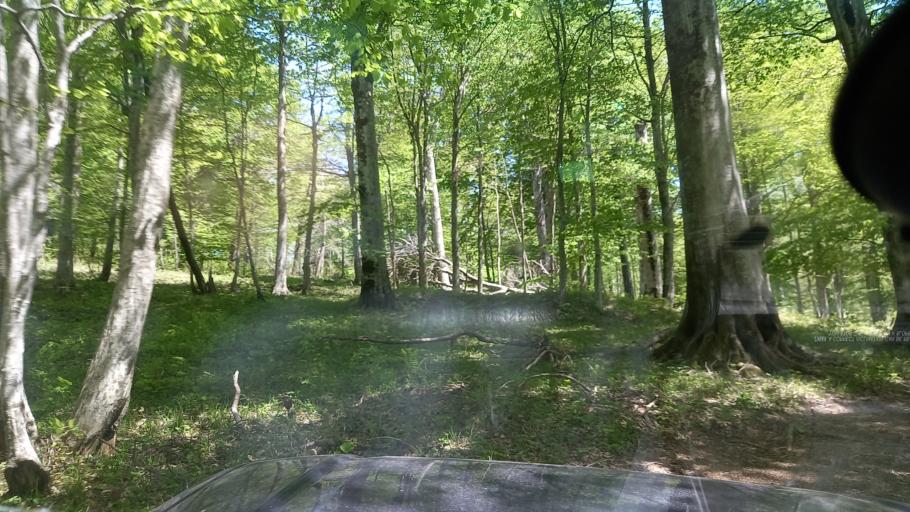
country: RU
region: Krasnodarskiy
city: Tuapse
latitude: 44.2479
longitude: 39.2898
